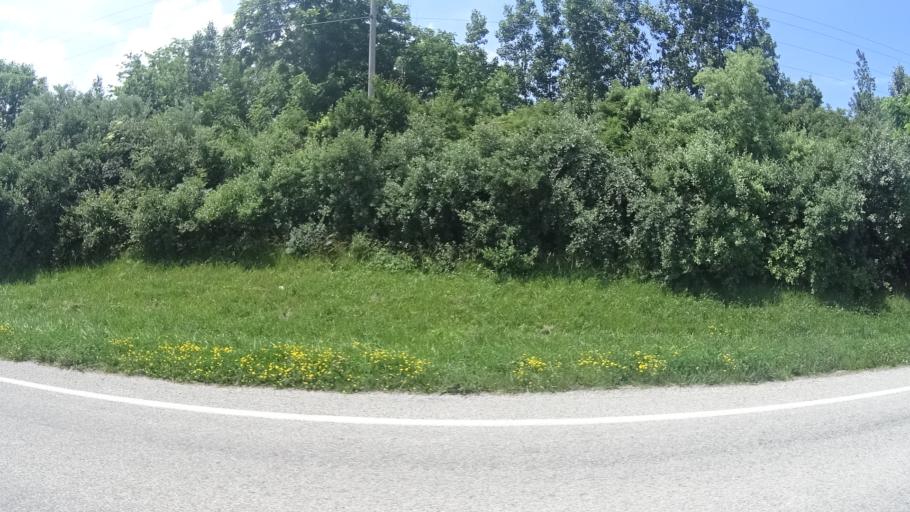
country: US
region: Ohio
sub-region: Erie County
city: Huron
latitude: 41.3644
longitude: -82.5473
